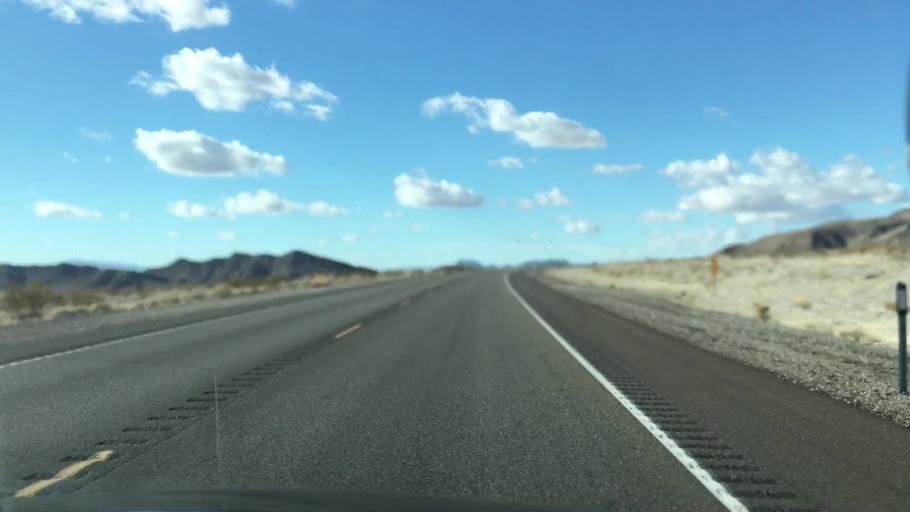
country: US
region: Nevada
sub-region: Nye County
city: Pahrump
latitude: 36.5737
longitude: -116.1840
